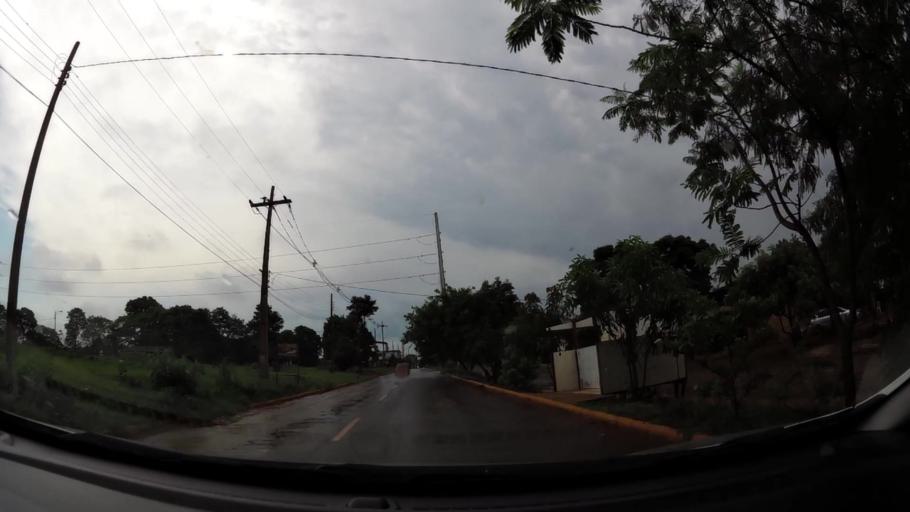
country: PY
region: Alto Parana
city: Presidente Franco
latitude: -25.5270
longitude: -54.6670
